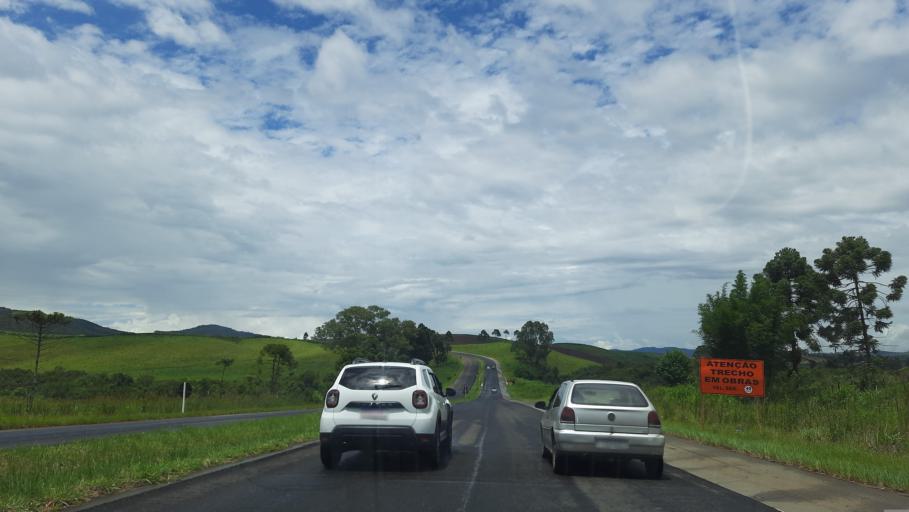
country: BR
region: Minas Gerais
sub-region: Pocos De Caldas
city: Pocos de Caldas
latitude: -21.8374
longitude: -46.6740
